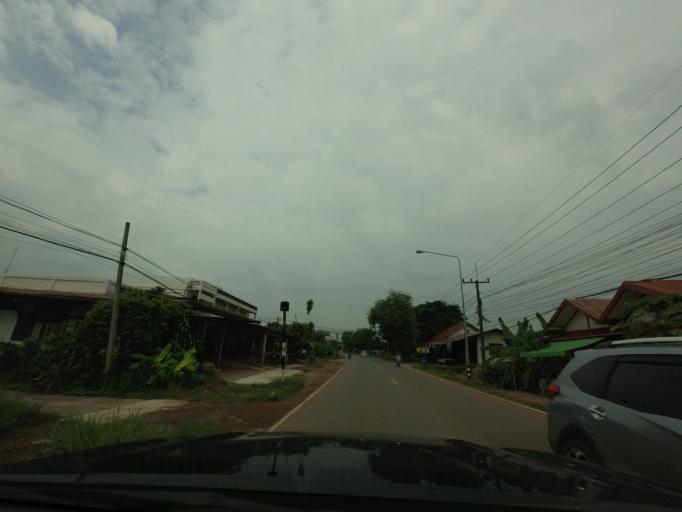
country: TH
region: Nong Khai
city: Tha Bo
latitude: 17.7999
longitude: 102.6650
